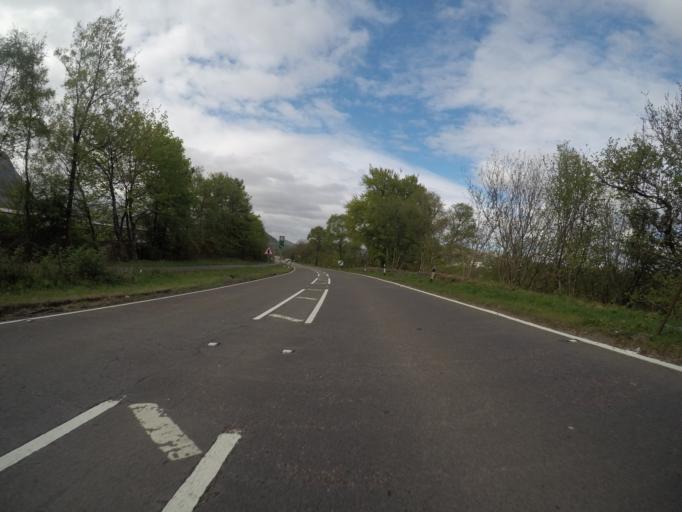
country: GB
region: Scotland
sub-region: Highland
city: Fort William
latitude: 56.8385
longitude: -5.0710
